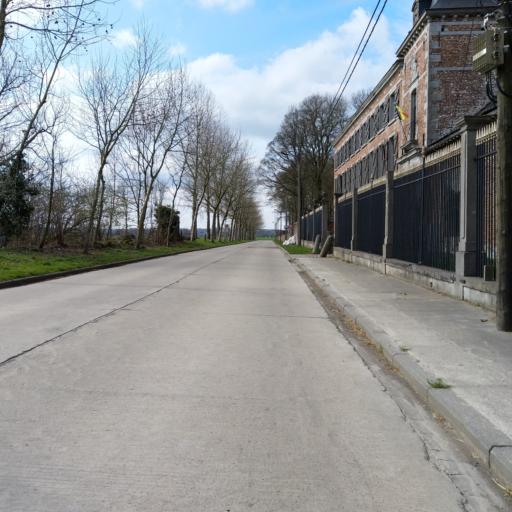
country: BE
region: Wallonia
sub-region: Province du Hainaut
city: Soignies
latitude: 50.5163
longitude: 4.0444
